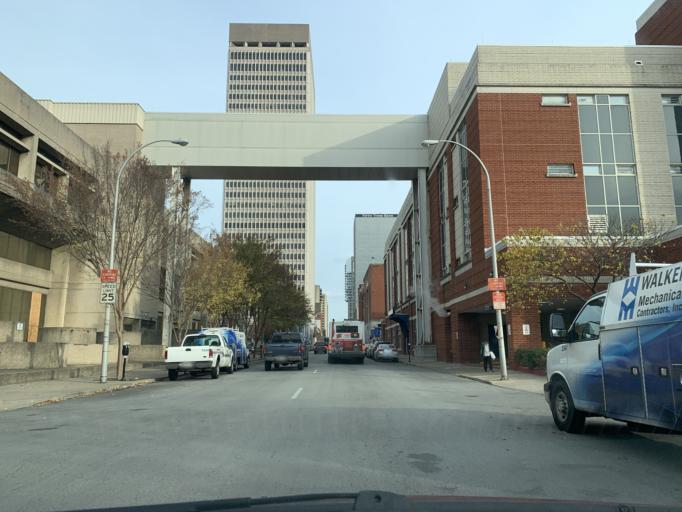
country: US
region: Kentucky
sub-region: Jefferson County
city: Louisville
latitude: 38.2536
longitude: -85.7617
